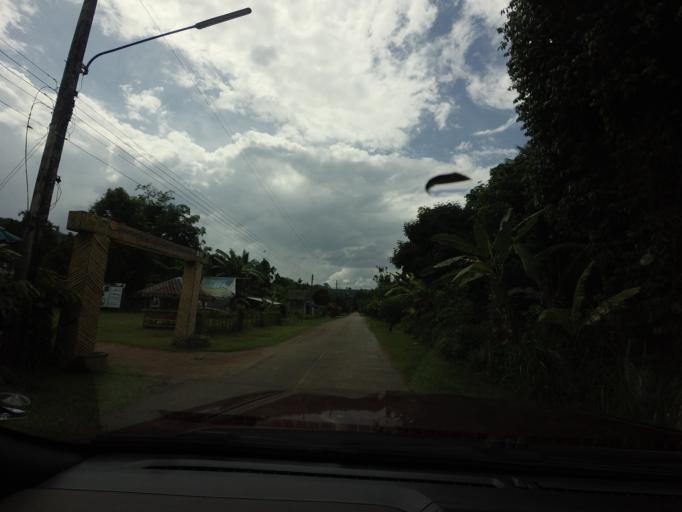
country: TH
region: Narathiwat
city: Sukhirin
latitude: 5.9229
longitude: 101.6419
